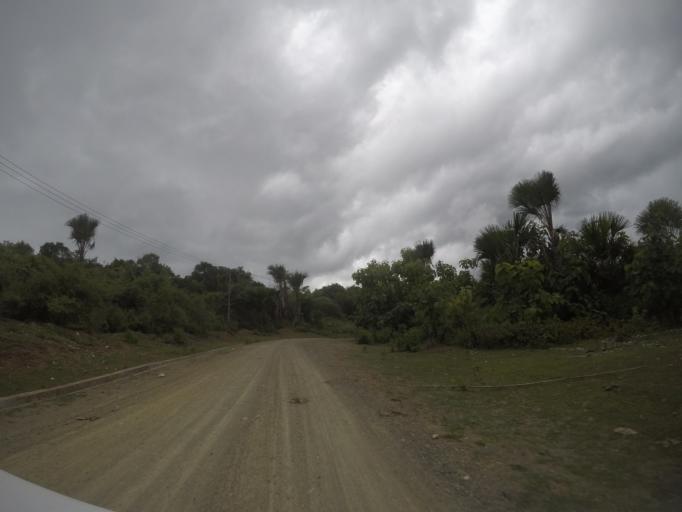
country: TL
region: Bobonaro
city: Maliana
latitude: -8.8498
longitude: 125.0727
